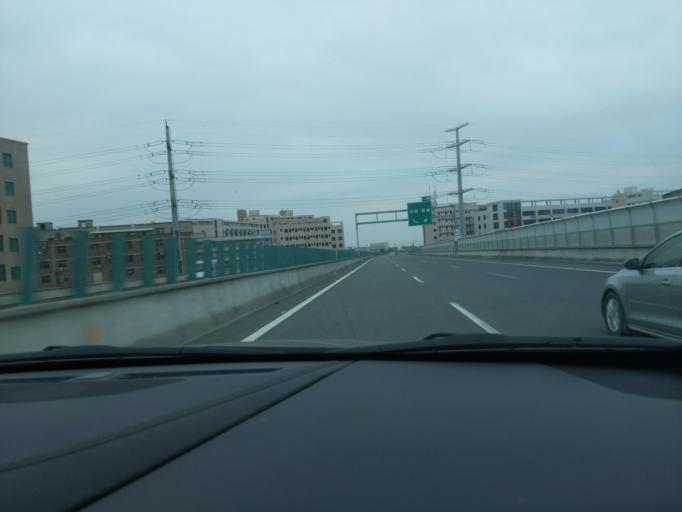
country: CN
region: Fujian
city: Shishi
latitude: 24.7597
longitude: 118.6114
